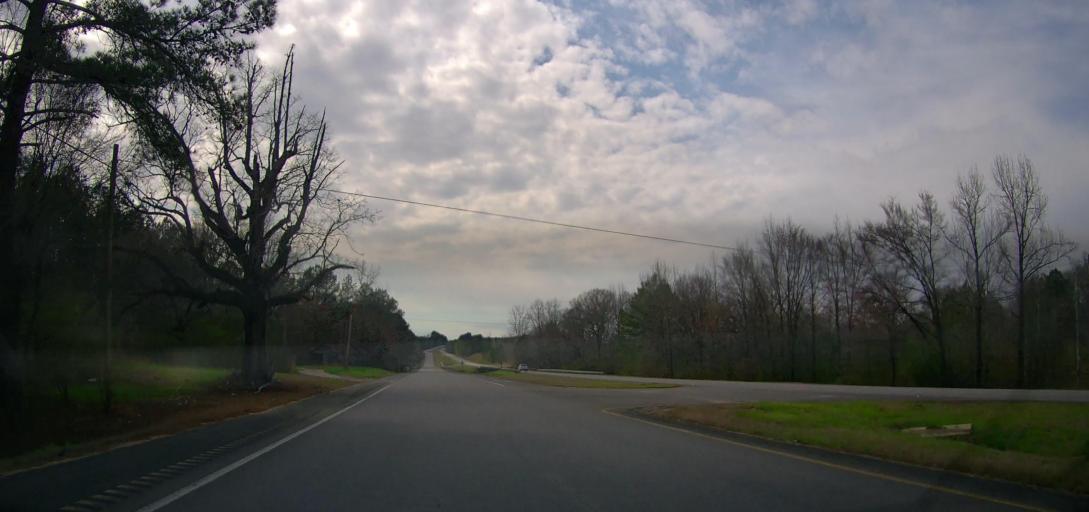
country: US
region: Alabama
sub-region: Marion County
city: Winfield
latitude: 33.9296
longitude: -87.6780
